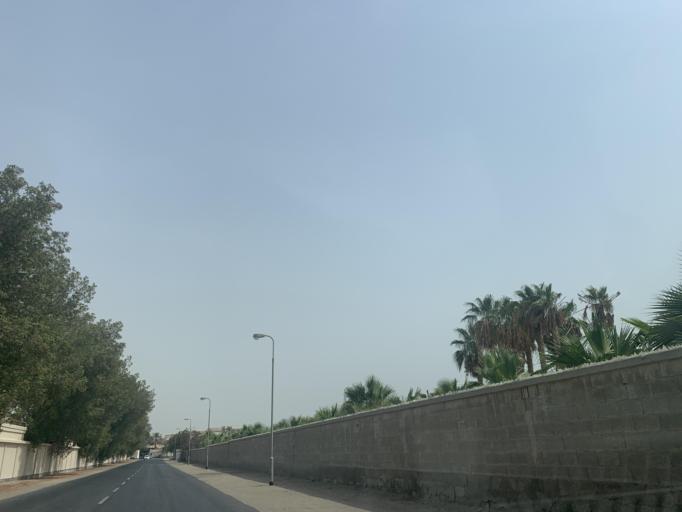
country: BH
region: Manama
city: Jidd Hafs
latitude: 26.2031
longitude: 50.4720
